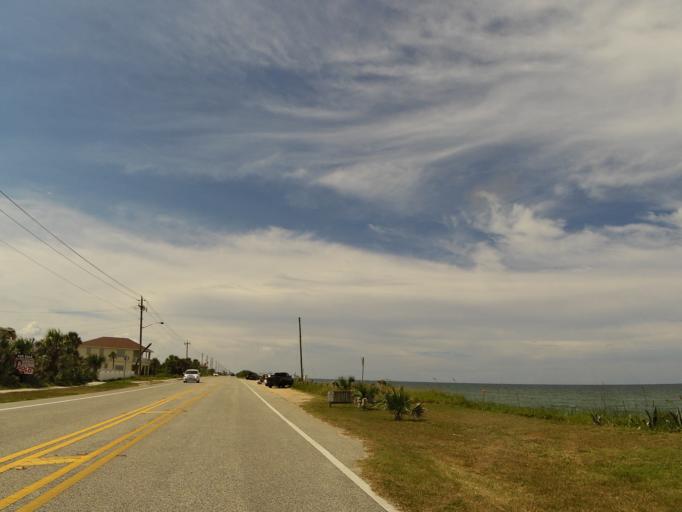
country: US
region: Florida
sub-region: Volusia County
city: Ormond-by-the-Sea
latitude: 29.3833
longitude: -81.0827
